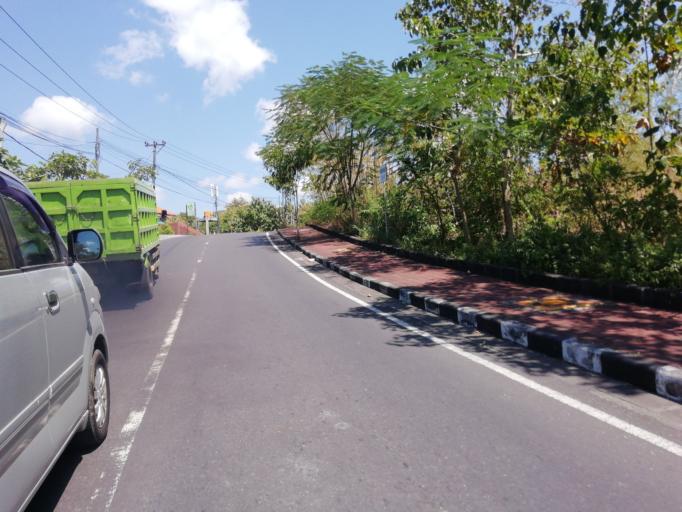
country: ID
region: Bali
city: Jimbaran
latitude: -8.7975
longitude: 115.1750
